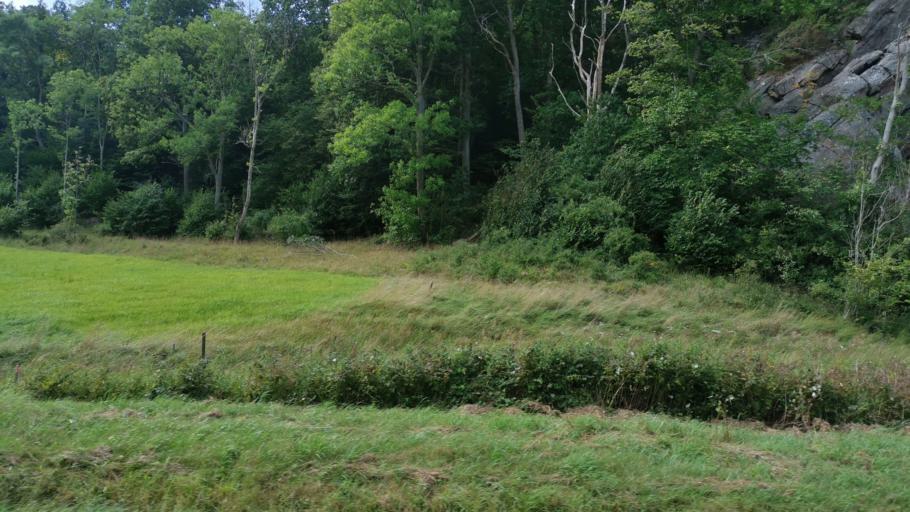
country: SE
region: Vaestra Goetaland
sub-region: Sotenas Kommun
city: Hunnebostrand
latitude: 58.5492
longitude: 11.2800
